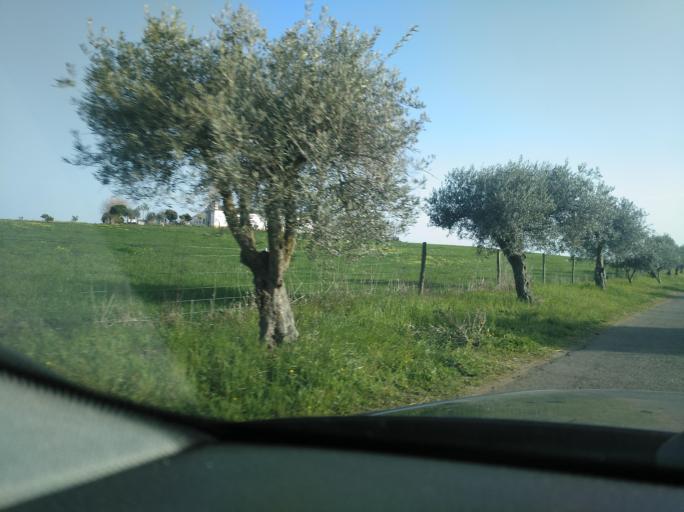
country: PT
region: Portalegre
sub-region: Campo Maior
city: Campo Maior
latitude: 39.0151
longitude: -7.0401
